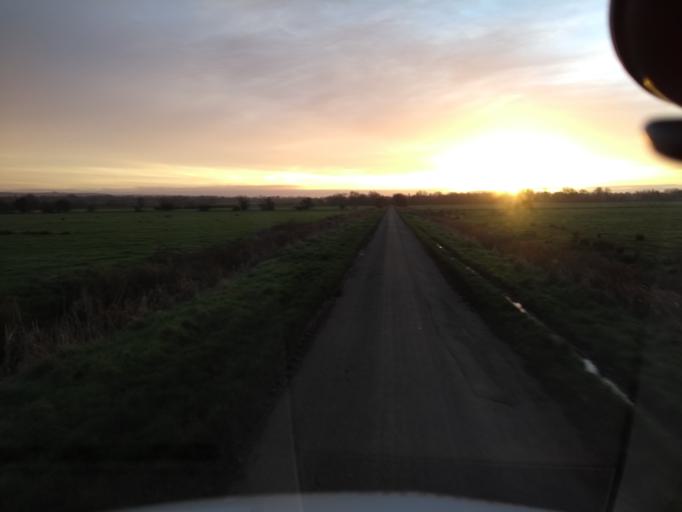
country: GB
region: England
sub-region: Somerset
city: Wedmore
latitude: 51.2295
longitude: -2.8653
